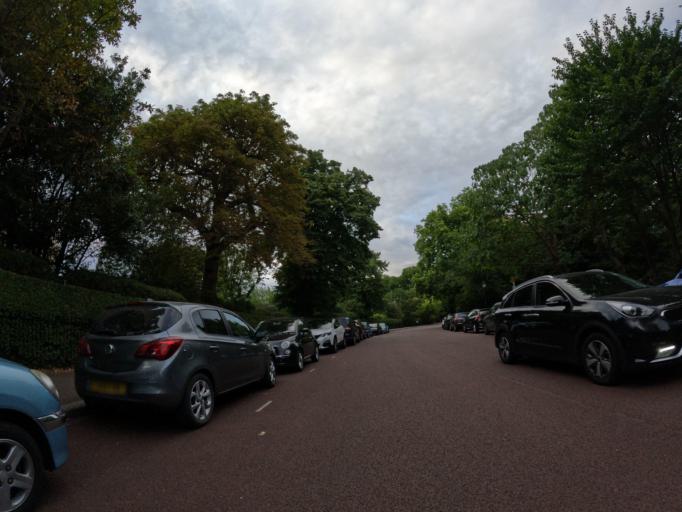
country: GB
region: England
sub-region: Greater London
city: Camden Town
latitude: 51.5274
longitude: -0.1560
